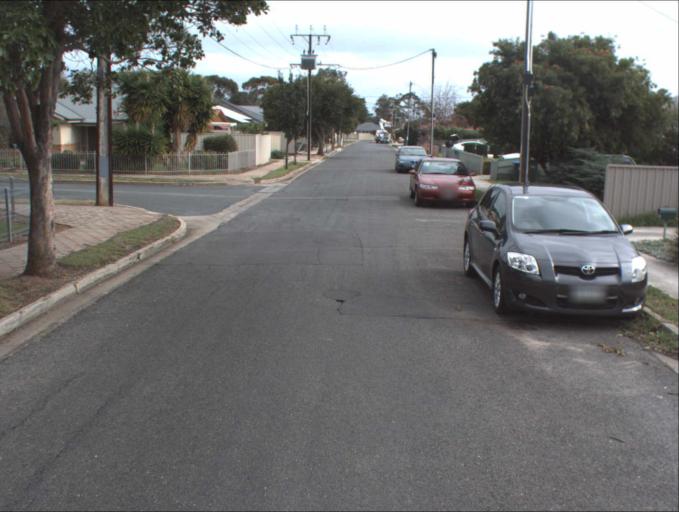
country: AU
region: South Australia
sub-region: Salisbury
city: Ingle Farm
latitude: -34.8511
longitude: 138.6250
